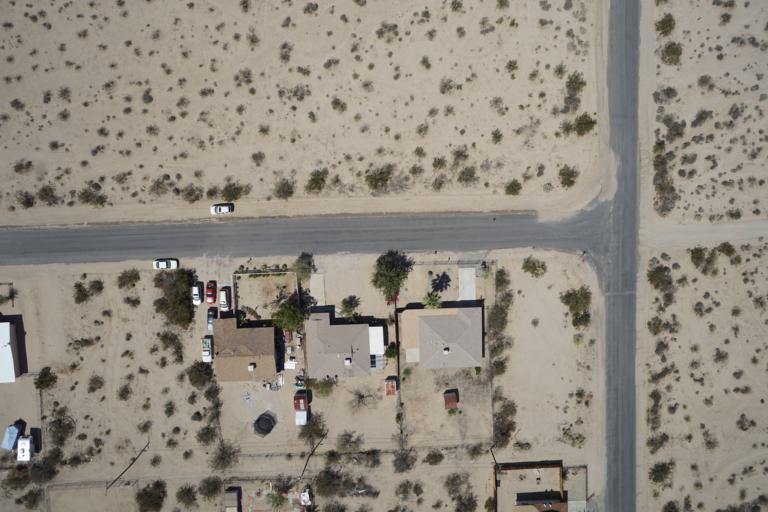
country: US
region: California
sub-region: San Bernardino County
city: Twentynine Palms
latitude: 34.1318
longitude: -116.0323
